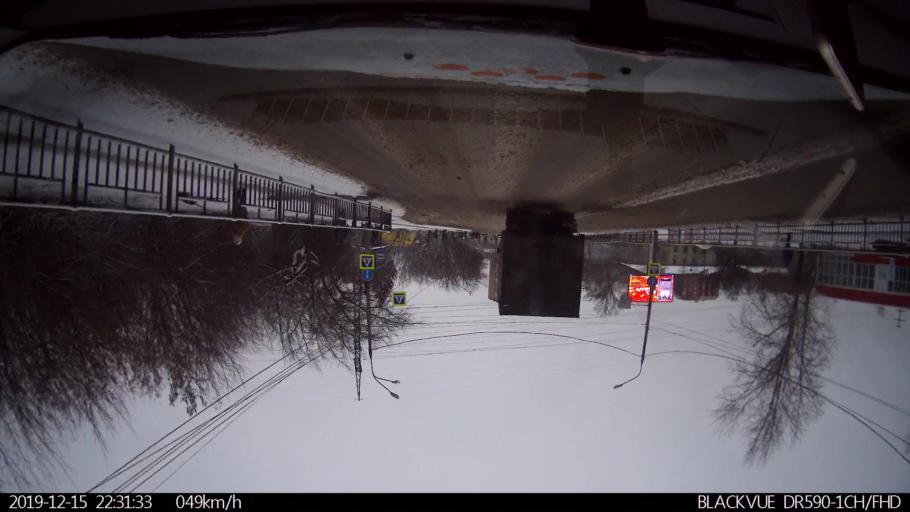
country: RU
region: Nizjnij Novgorod
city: Gorbatovka
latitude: 56.3458
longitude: 43.8430
